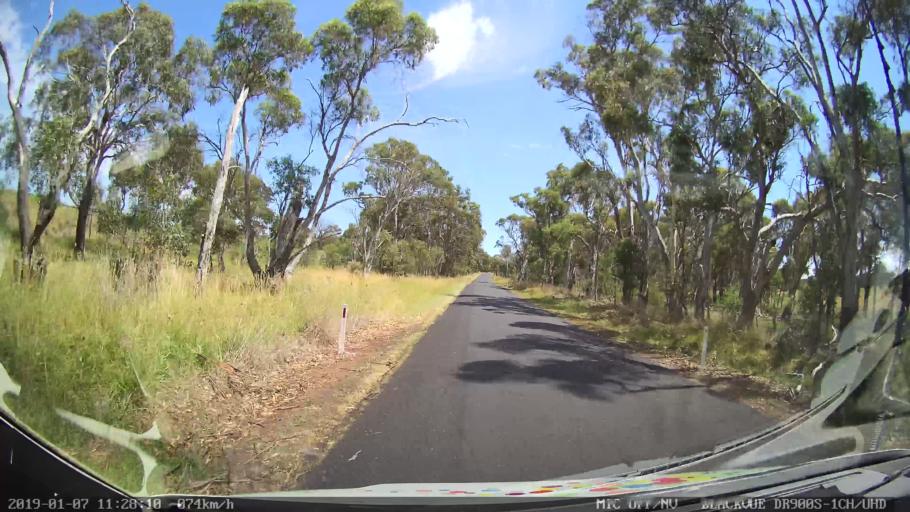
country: AU
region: New South Wales
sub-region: Armidale Dumaresq
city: Armidale
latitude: -30.4512
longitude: 151.5679
